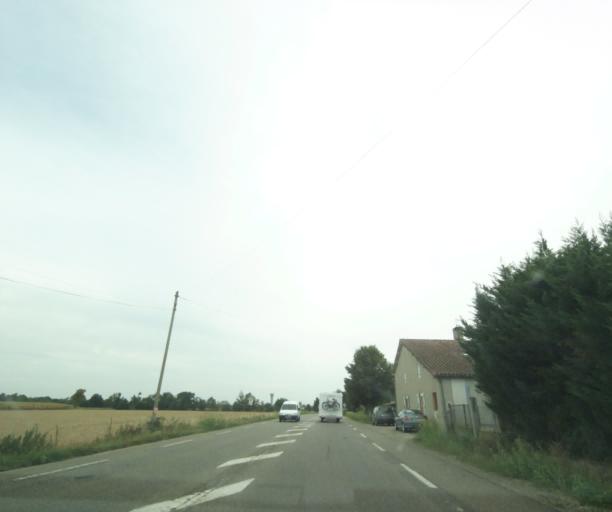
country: FR
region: Midi-Pyrenees
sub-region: Departement du Tarn-et-Garonne
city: Saint-Porquier
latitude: 44.0001
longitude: 1.1838
